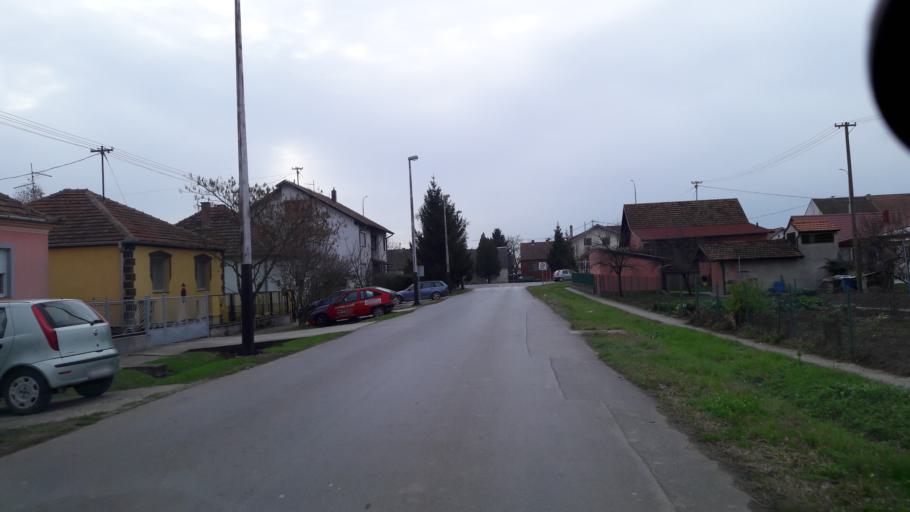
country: HR
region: Osjecko-Baranjska
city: Cepin
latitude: 45.5261
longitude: 18.5850
